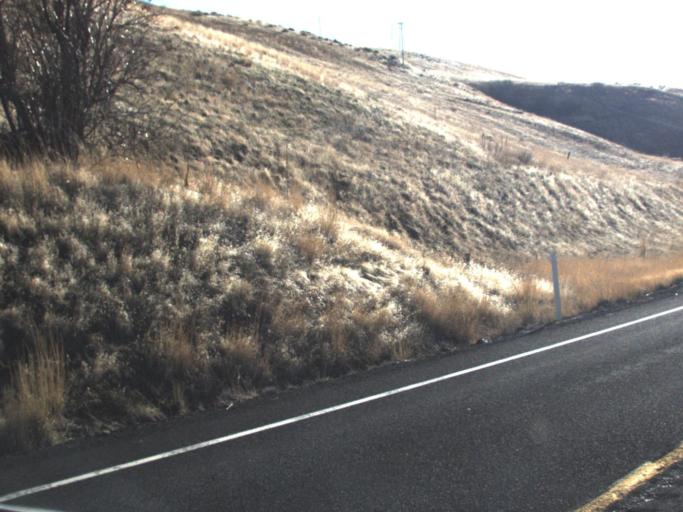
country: US
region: Washington
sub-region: Garfield County
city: Pomeroy
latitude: 46.4553
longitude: -117.4719
